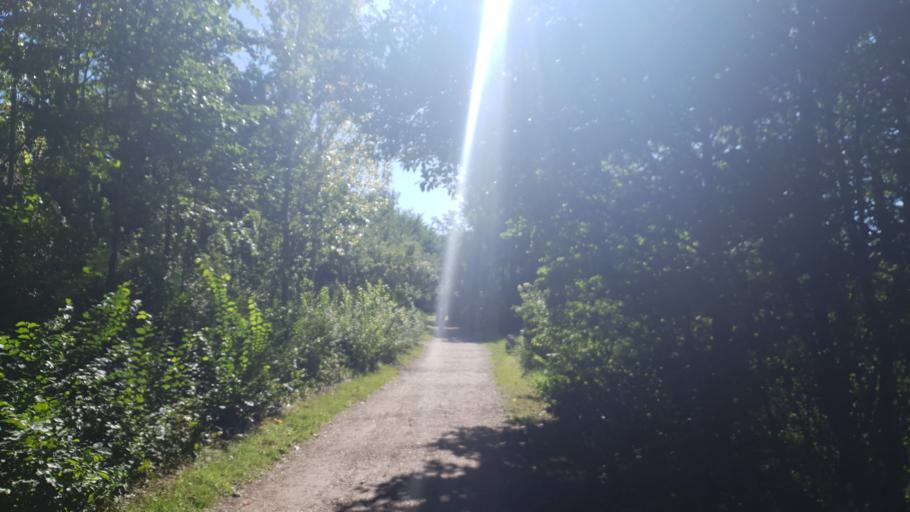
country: DK
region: Zealand
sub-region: Roskilde Kommune
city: Roskilde
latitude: 55.6330
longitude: 12.0829
